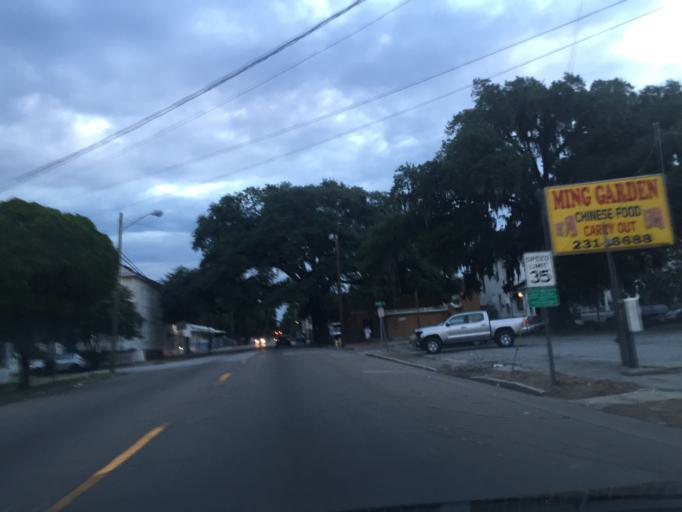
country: US
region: Georgia
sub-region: Chatham County
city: Savannah
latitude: 32.0545
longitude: -81.1057
